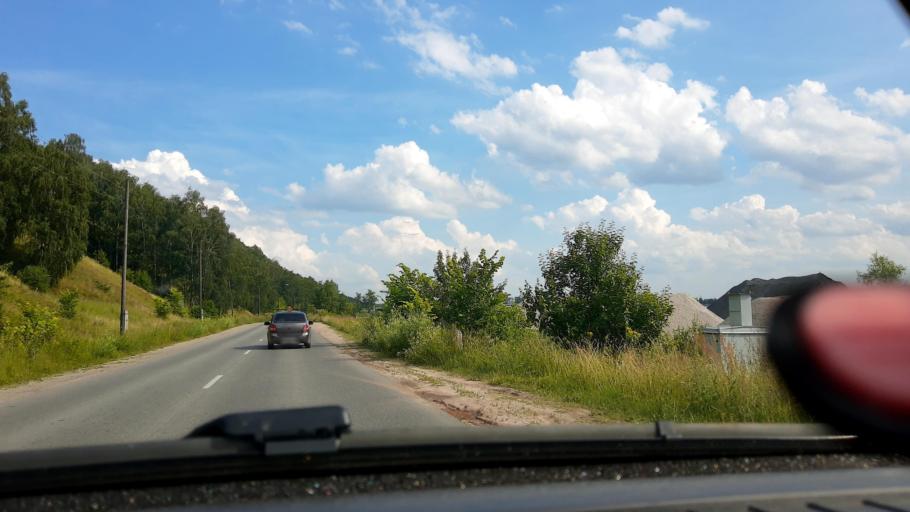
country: RU
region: Nizjnij Novgorod
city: Gorodets
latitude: 56.6767
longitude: 43.4421
